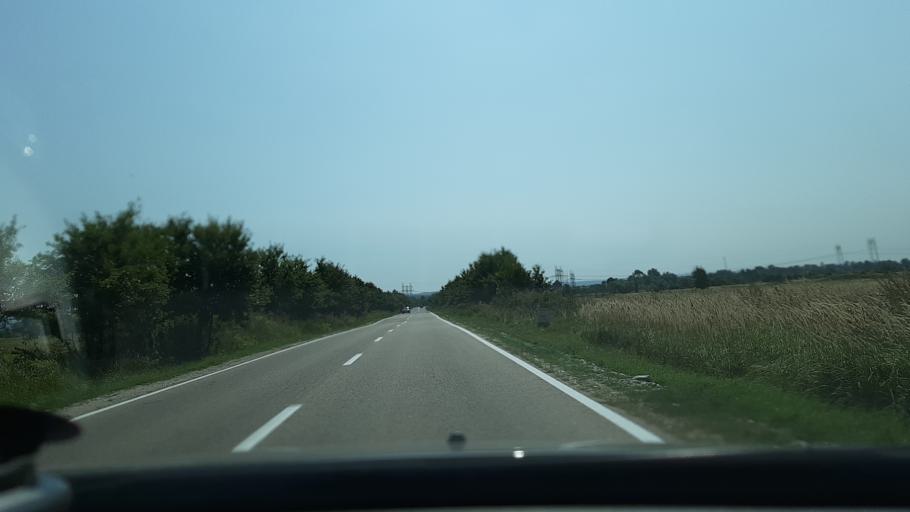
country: RO
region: Gorj
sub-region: Comuna Targu Carbunesti
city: Pojogeni
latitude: 45.0048
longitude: 23.4855
